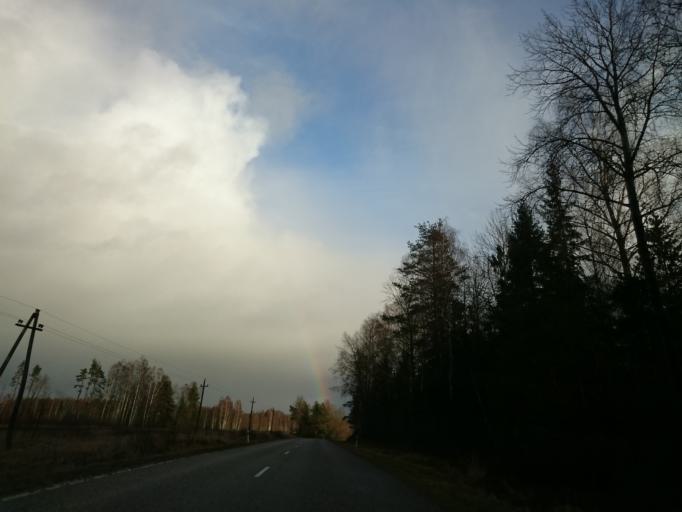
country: LV
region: Skrunda
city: Skrunda
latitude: 56.6826
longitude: 21.9377
